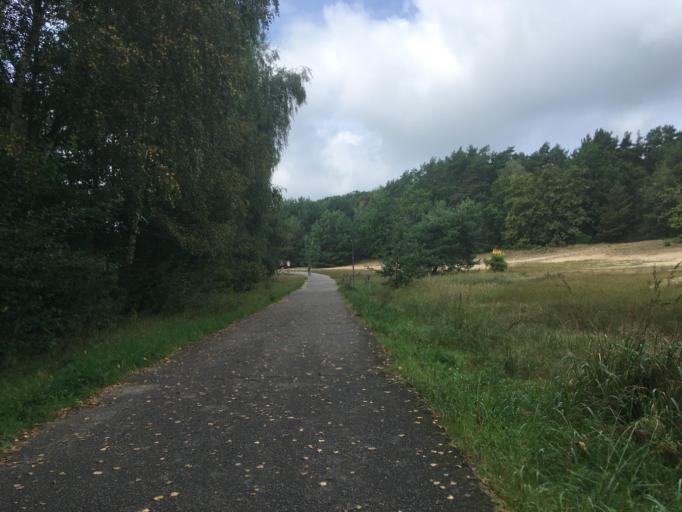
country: DE
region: Berlin
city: Lubars
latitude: 52.6273
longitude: 13.3564
